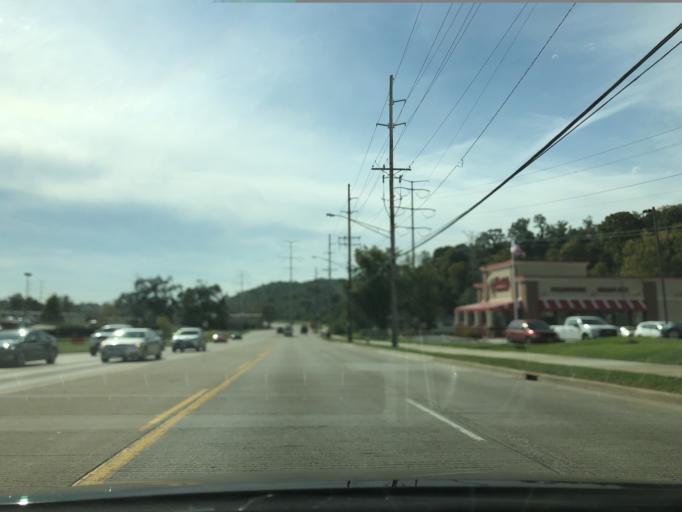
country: US
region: Ohio
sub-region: Hamilton County
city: Fairfax
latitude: 39.1471
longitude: -84.4048
